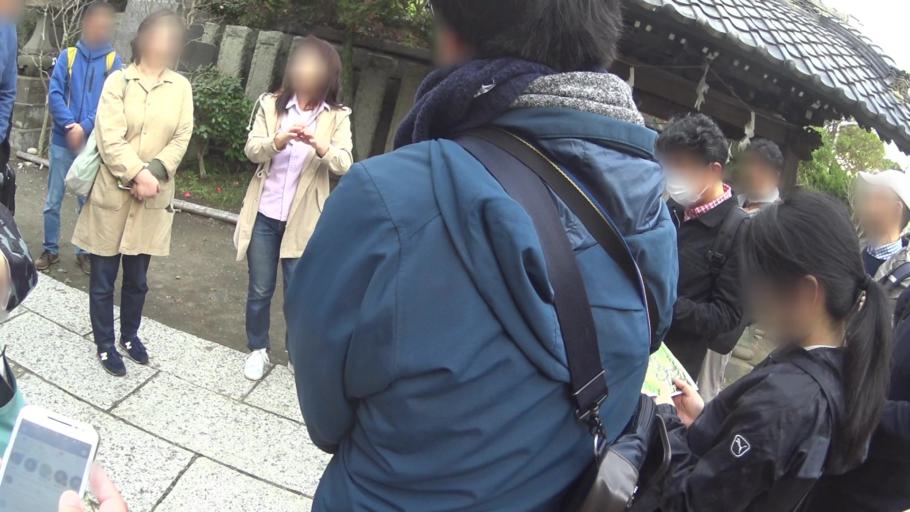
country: JP
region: Kanagawa
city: Fujisawa
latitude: 35.3125
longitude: 139.4893
